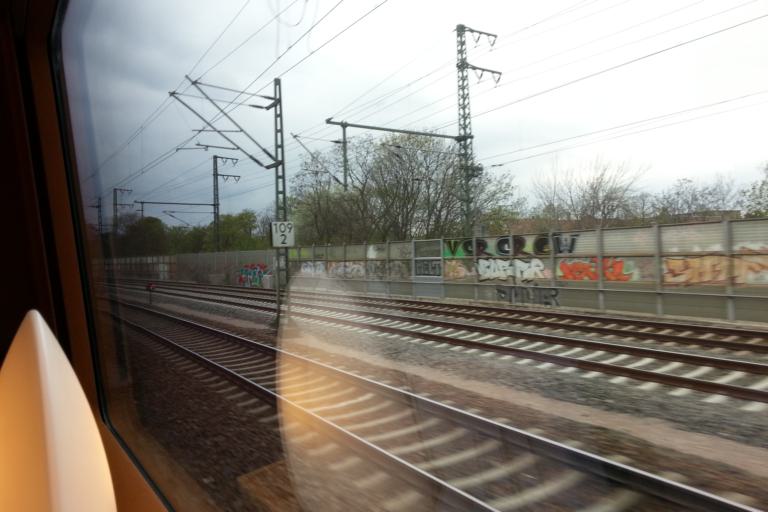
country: DE
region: Thuringia
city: Erfurt
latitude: 50.9692
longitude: 11.0279
